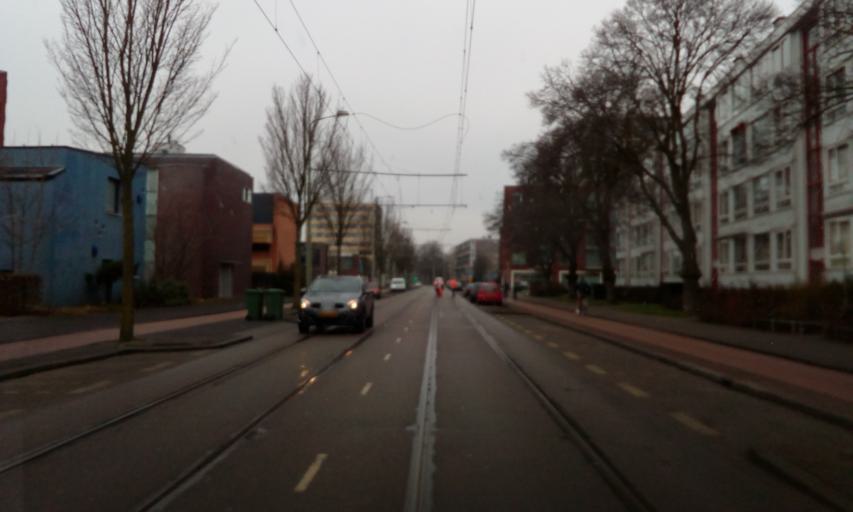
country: NL
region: South Holland
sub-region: Gemeente Westland
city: Kwintsheul
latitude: 52.0487
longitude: 4.2661
